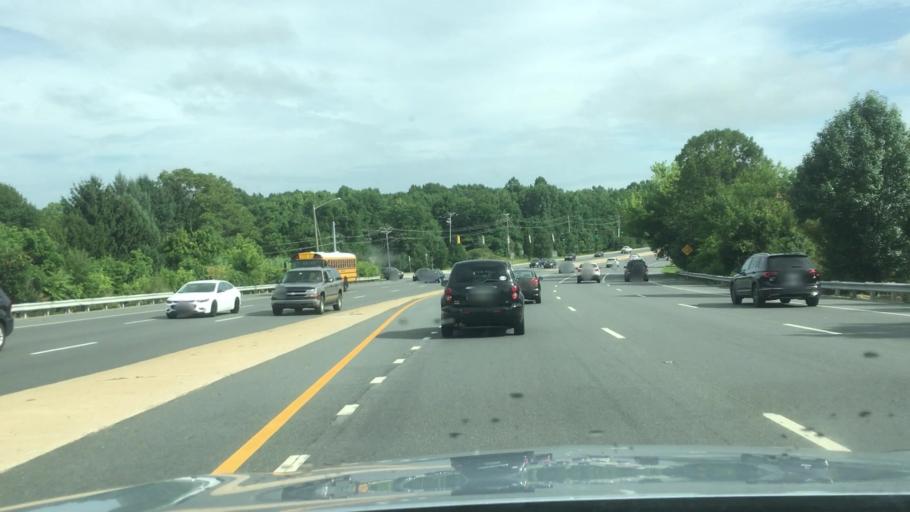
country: US
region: Delaware
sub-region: New Castle County
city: Newport
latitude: 39.7009
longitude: -75.6521
